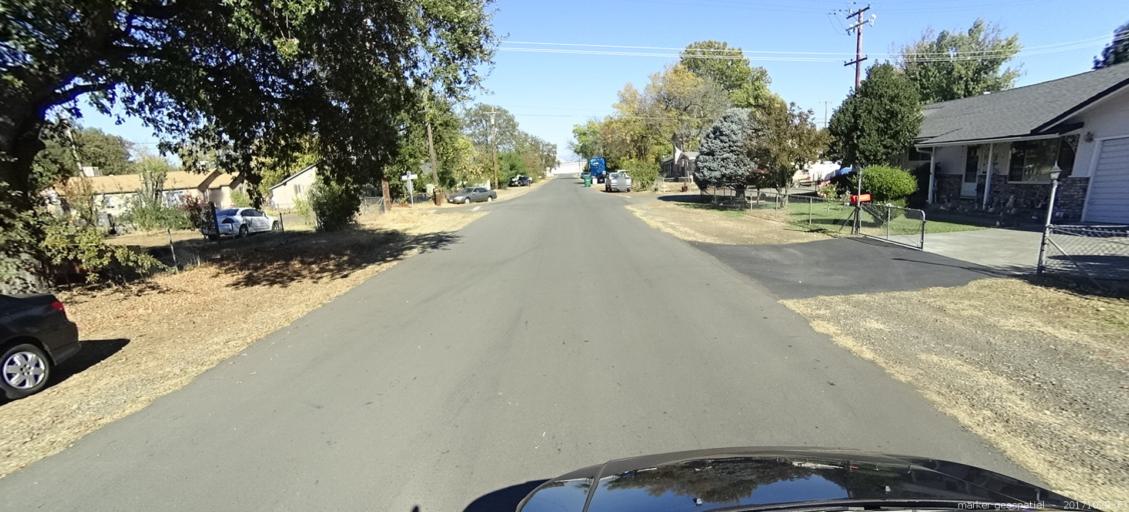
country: US
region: California
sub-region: Shasta County
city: Anderson
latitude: 40.4683
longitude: -122.3337
